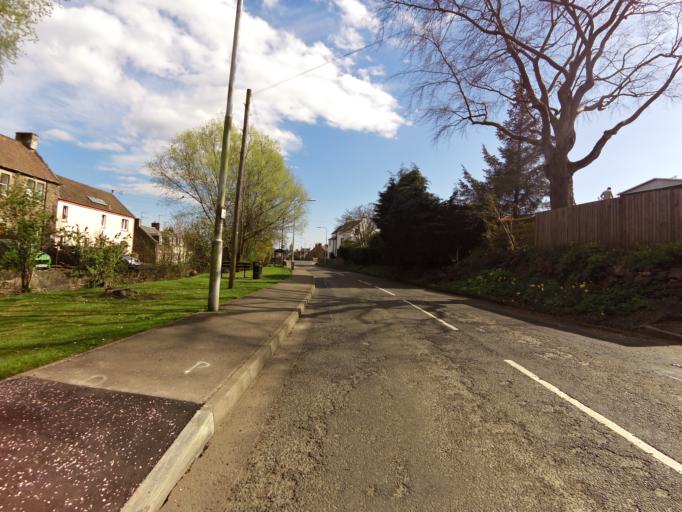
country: GB
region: Scotland
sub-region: Fife
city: Auchtermuchty
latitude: 56.2957
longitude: -3.2371
